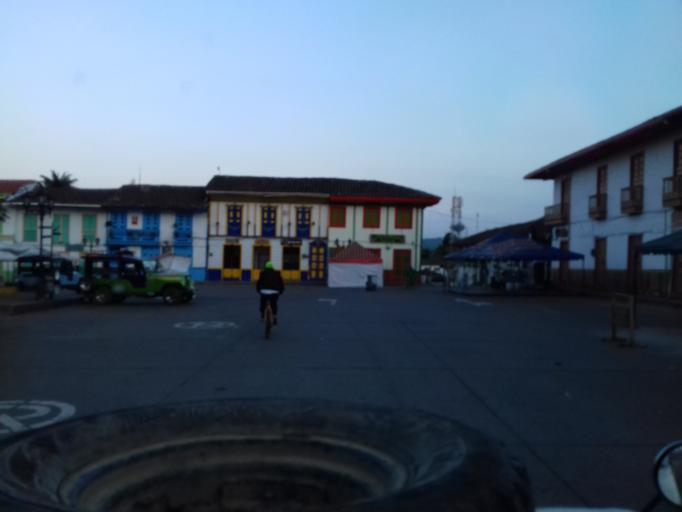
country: CO
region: Quindio
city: Salento
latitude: 4.6373
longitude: -75.5695
